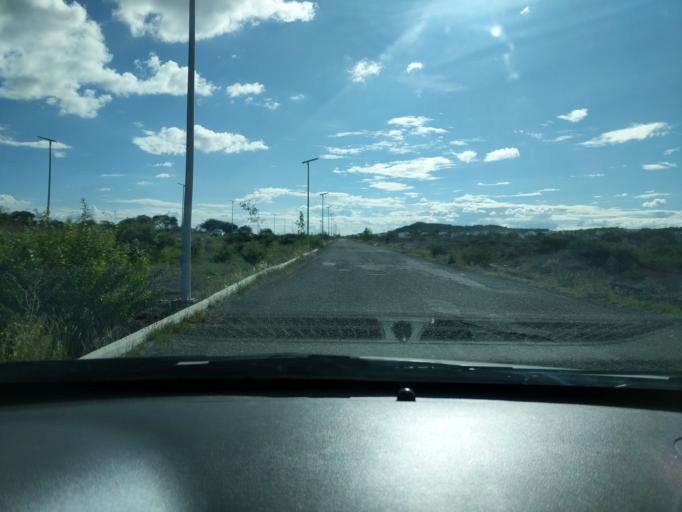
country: MX
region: Queretaro
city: La Canada
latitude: 20.5969
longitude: -100.3020
